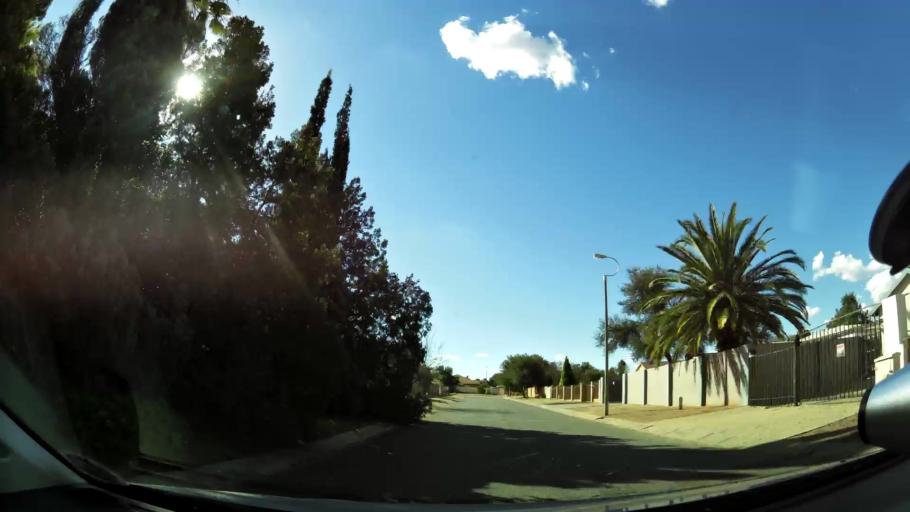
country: ZA
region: North-West
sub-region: Dr Kenneth Kaunda District Municipality
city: Klerksdorp
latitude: -26.8344
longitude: 26.6534
